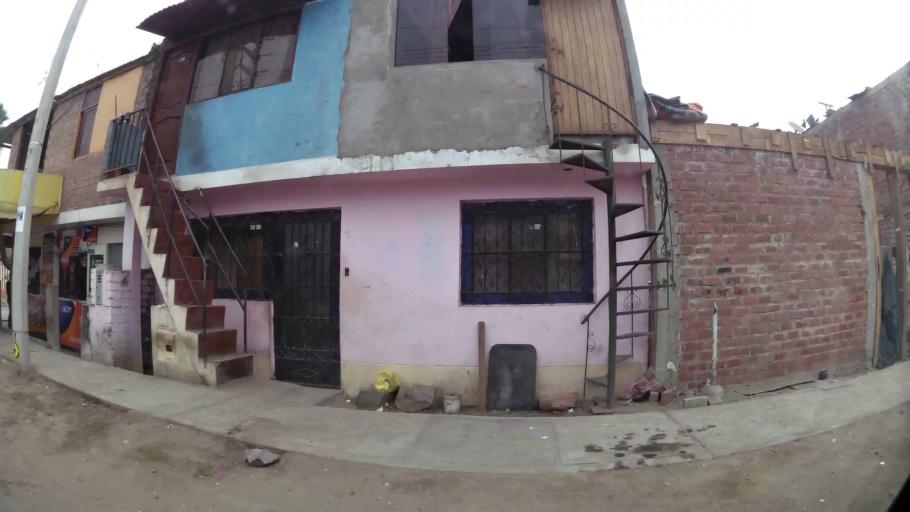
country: PE
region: Lima
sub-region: Lima
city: Surco
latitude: -12.2222
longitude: -76.9467
